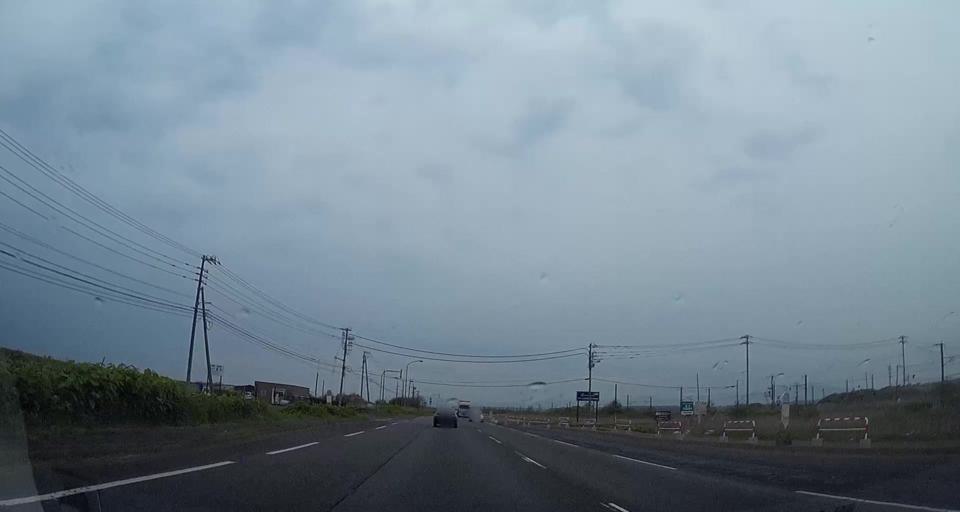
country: JP
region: Hokkaido
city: Shiraoi
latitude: 42.5842
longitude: 141.4353
